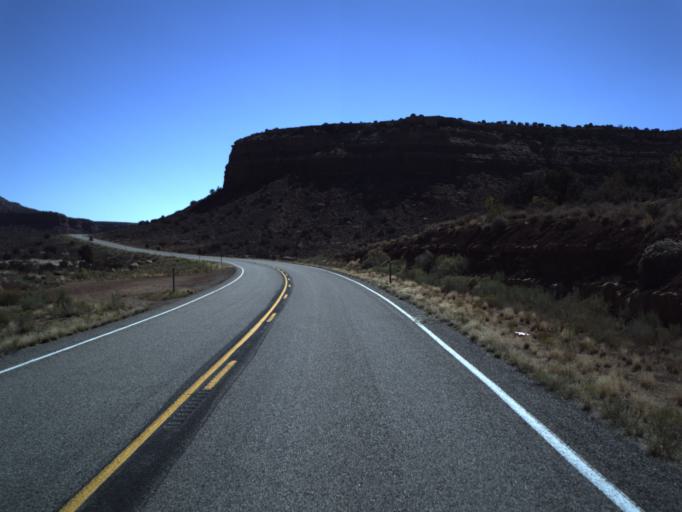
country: US
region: Utah
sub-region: San Juan County
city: Blanding
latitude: 37.7325
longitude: -110.2582
